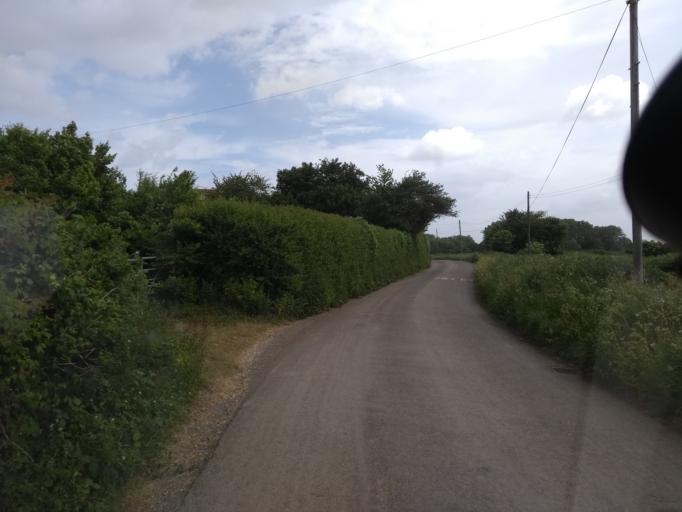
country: GB
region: England
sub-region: Somerset
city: Bishops Lydeard
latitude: 51.1755
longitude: -3.1800
